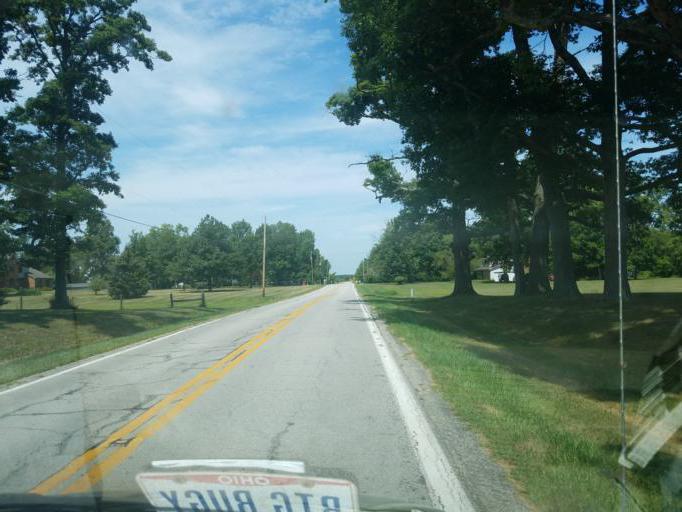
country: US
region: Ohio
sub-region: Madison County
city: Mount Sterling
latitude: 39.8229
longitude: -83.2363
